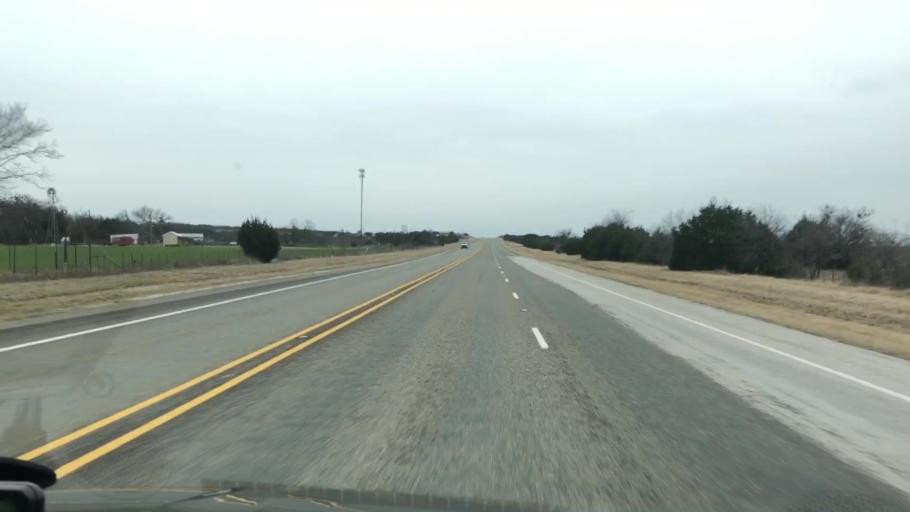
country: US
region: Texas
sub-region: Lampasas County
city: Lampasas
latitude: 31.1756
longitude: -98.1738
